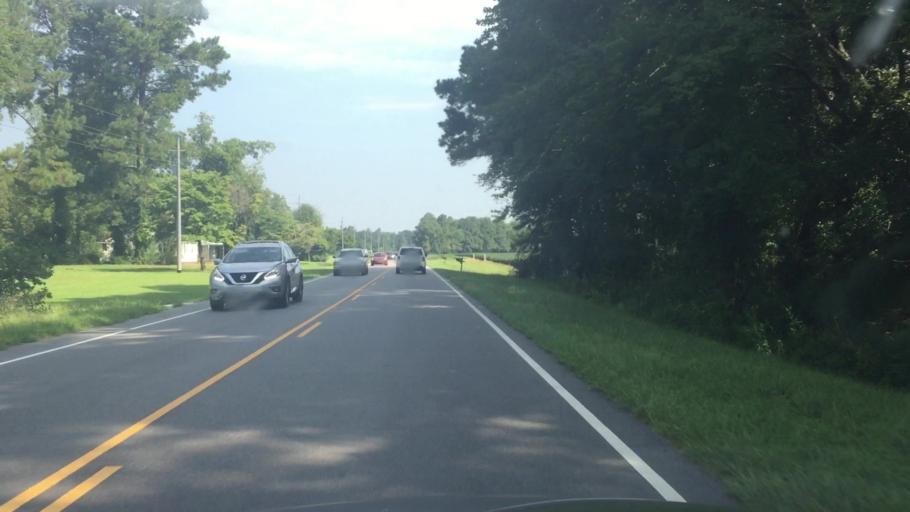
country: US
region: North Carolina
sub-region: Columbus County
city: Chadbourn
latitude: 34.3468
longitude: -78.8276
